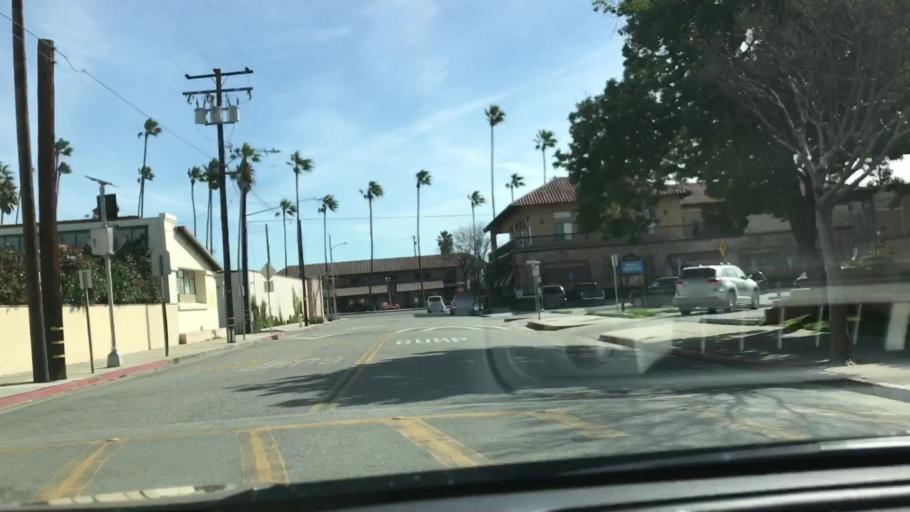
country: US
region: California
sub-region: Los Angeles County
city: San Fernando
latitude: 34.2808
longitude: -118.4429
